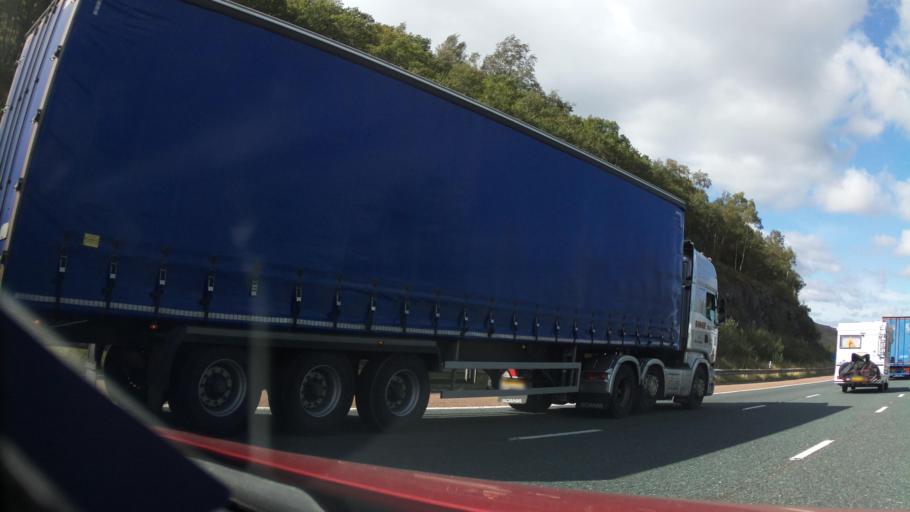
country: GB
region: England
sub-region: Cumbria
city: Sedbergh
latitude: 54.3843
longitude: -2.5831
